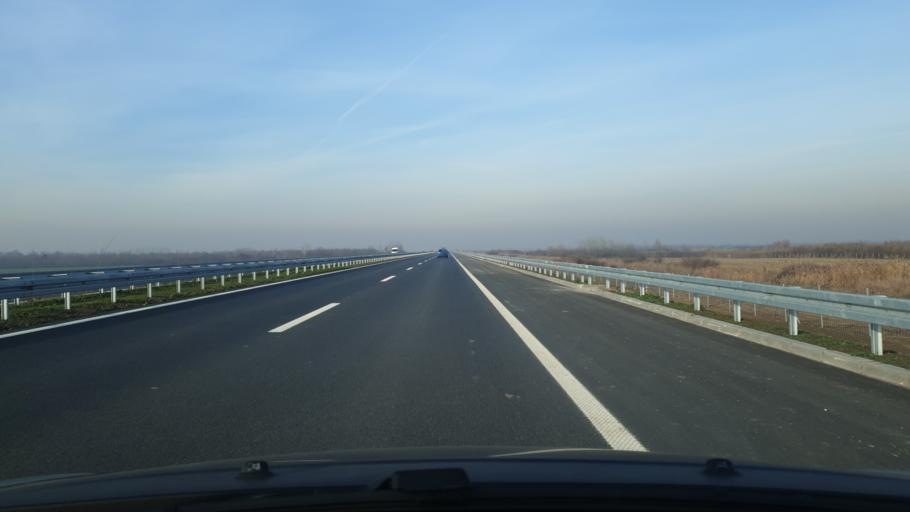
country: RS
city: Umka
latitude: 44.6983
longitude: 20.2650
